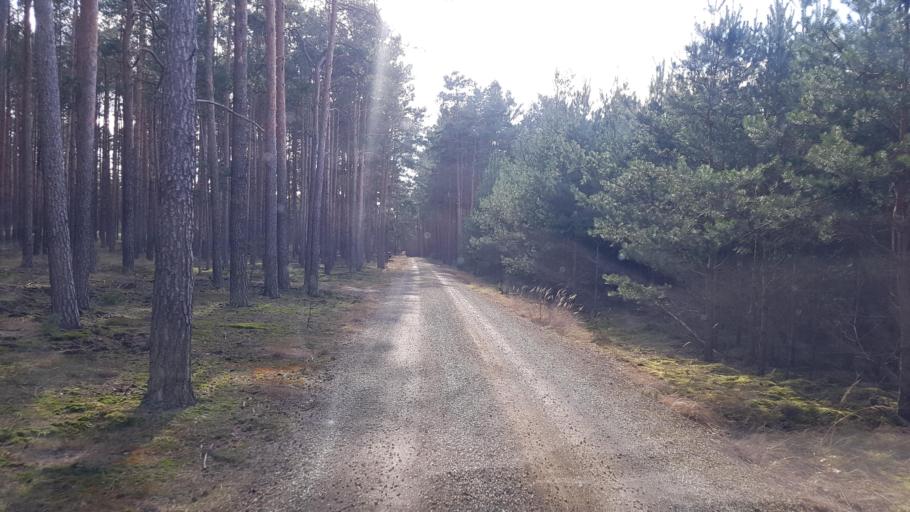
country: DE
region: Brandenburg
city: Schlieben
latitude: 51.6770
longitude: 13.3306
